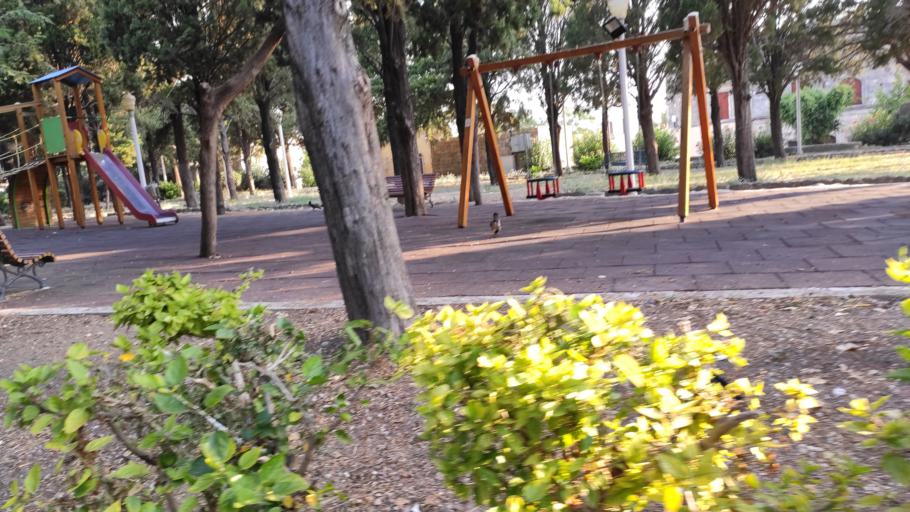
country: GR
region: South Aegean
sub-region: Nomos Dodekanisou
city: Rodos
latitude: 36.4423
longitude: 28.2315
